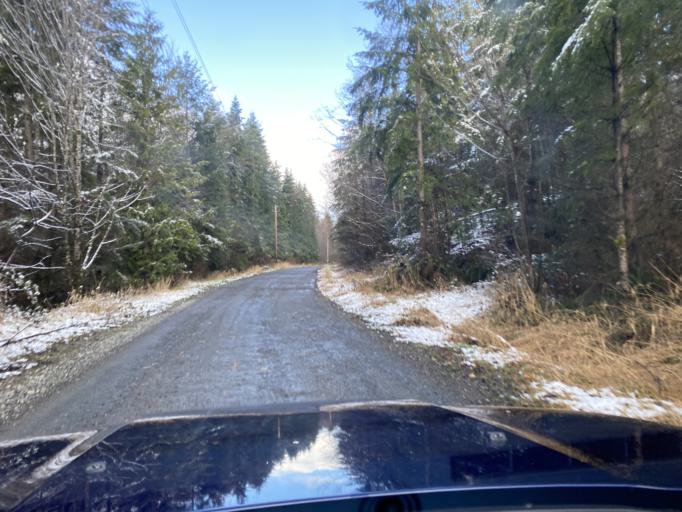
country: US
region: Washington
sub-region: King County
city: Snoqualmie
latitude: 47.4977
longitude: -121.8755
